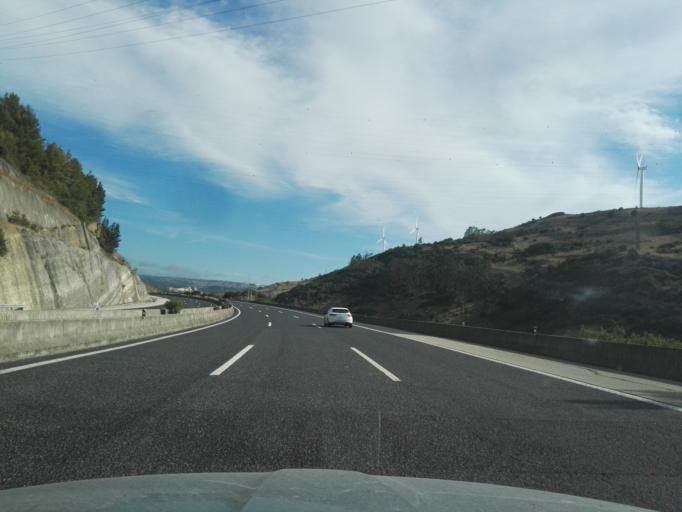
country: PT
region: Lisbon
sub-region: Loures
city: Bucelas
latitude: 38.8785
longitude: -9.1310
